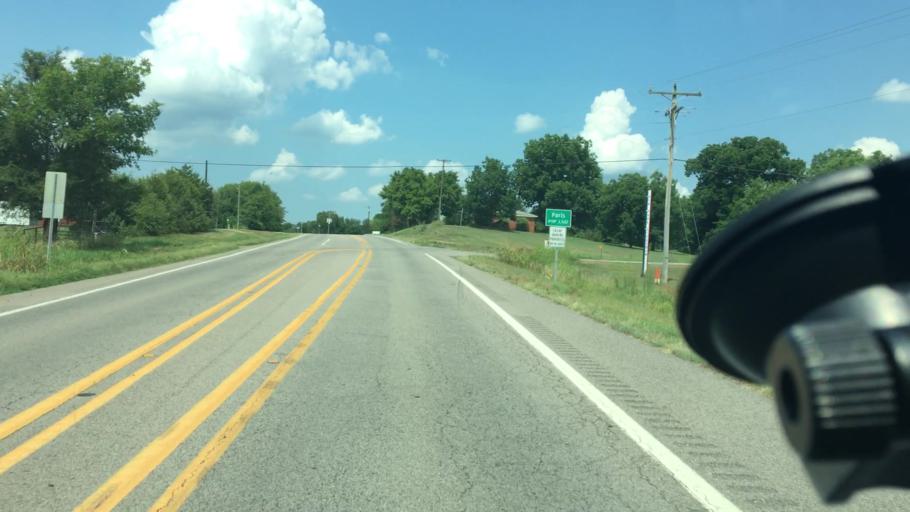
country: US
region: Arkansas
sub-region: Logan County
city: Paris
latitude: 35.2952
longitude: -93.6863
